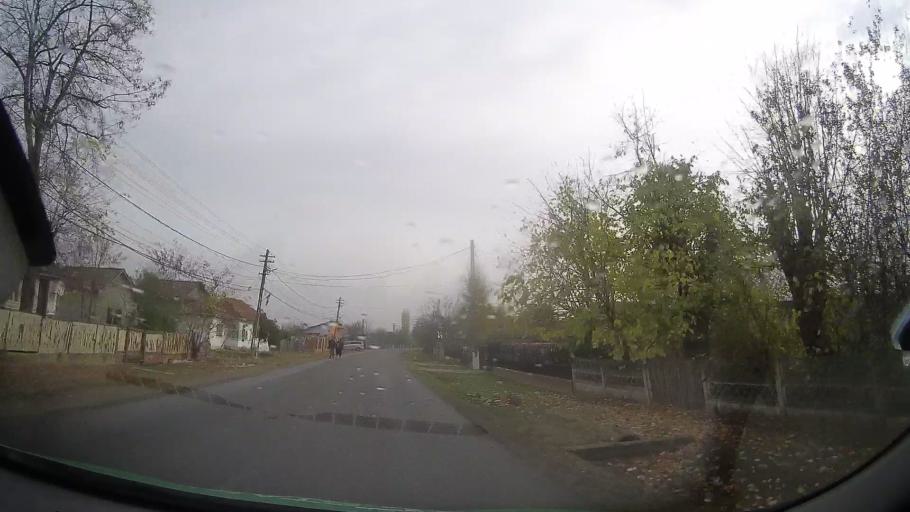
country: RO
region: Prahova
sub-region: Comuna Rafov
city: Palanca
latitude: 44.8444
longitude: 26.2339
